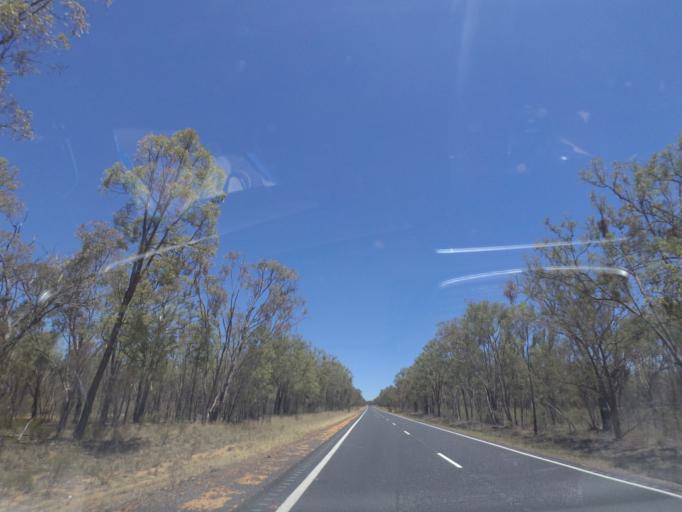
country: AU
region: New South Wales
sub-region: Warrumbungle Shire
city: Coonabarabran
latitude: -31.1668
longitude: 149.3636
